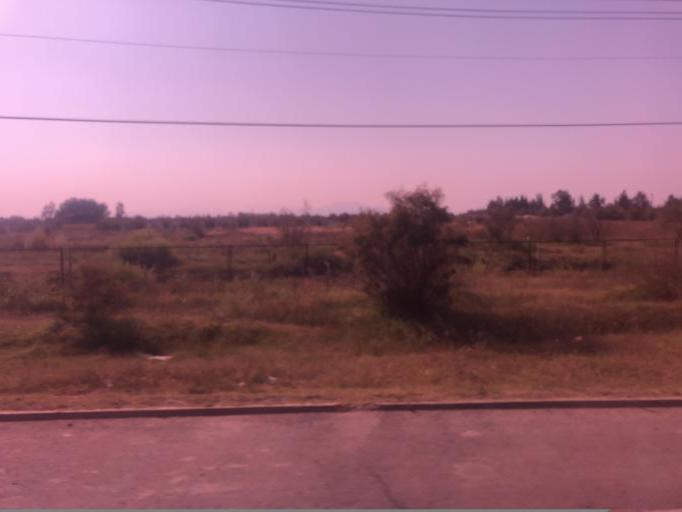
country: MX
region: Mexico
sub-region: Ciudad Nezahualcoyotl
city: Poligonos
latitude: 19.4776
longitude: -98.9812
